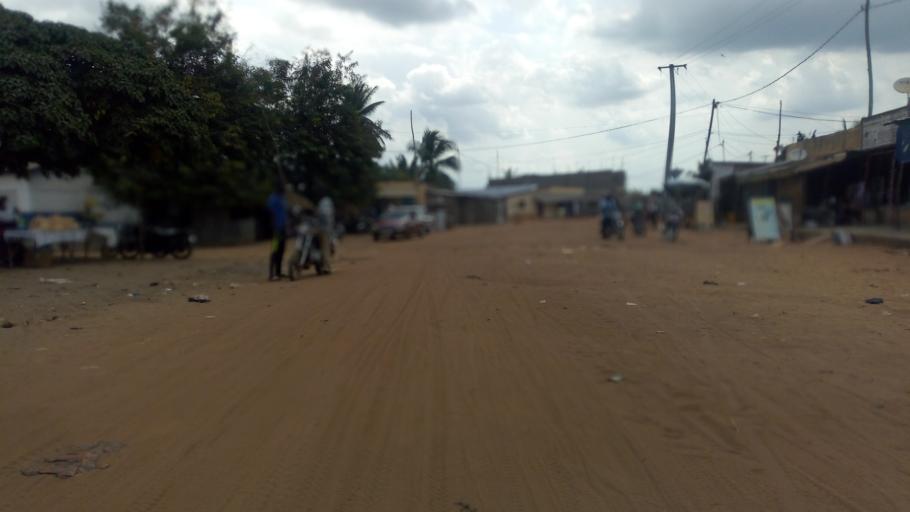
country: TG
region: Maritime
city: Tsevie
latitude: 6.3230
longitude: 1.2173
